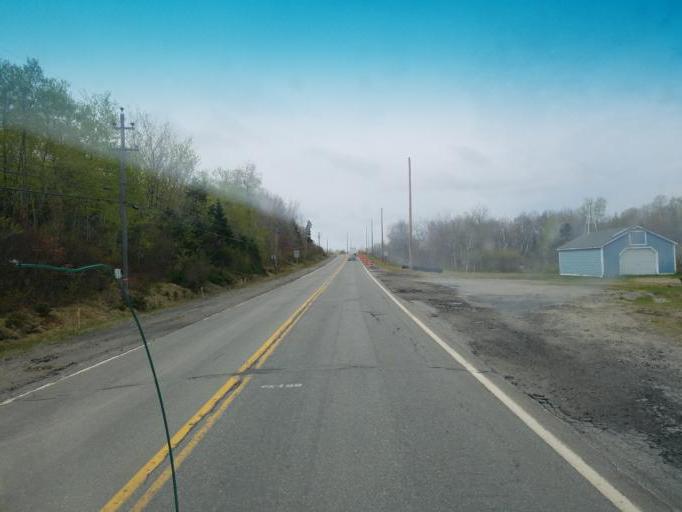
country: US
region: Maine
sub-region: Washington County
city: East Machias
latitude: 44.7829
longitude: -67.1914
